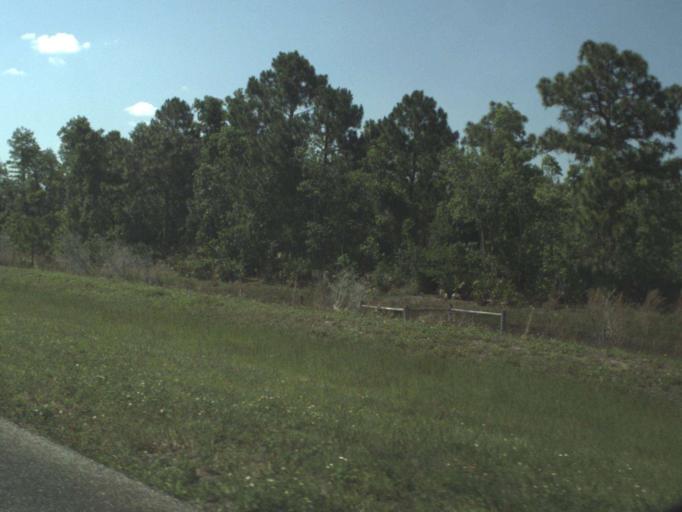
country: US
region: Florida
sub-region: Orange County
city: Christmas
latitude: 28.4743
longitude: -81.0157
